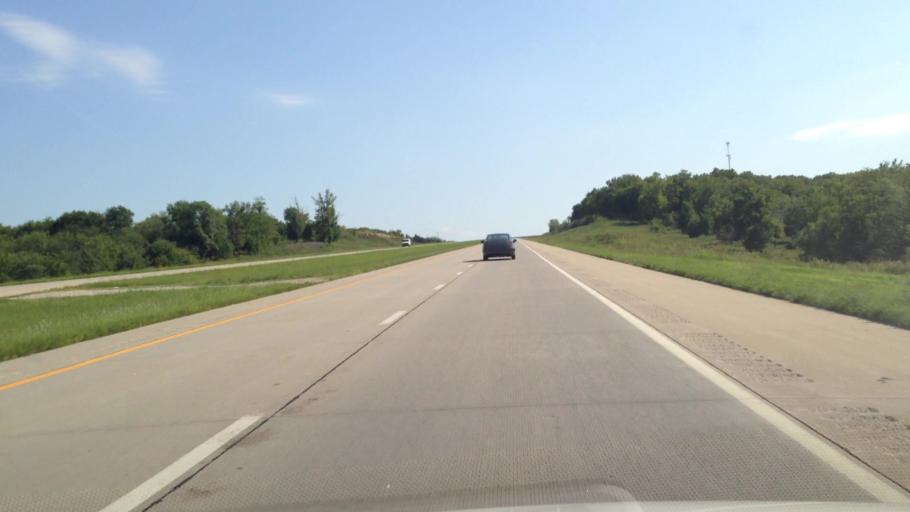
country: US
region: Kansas
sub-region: Linn County
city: Pleasanton
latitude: 38.1195
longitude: -94.7137
